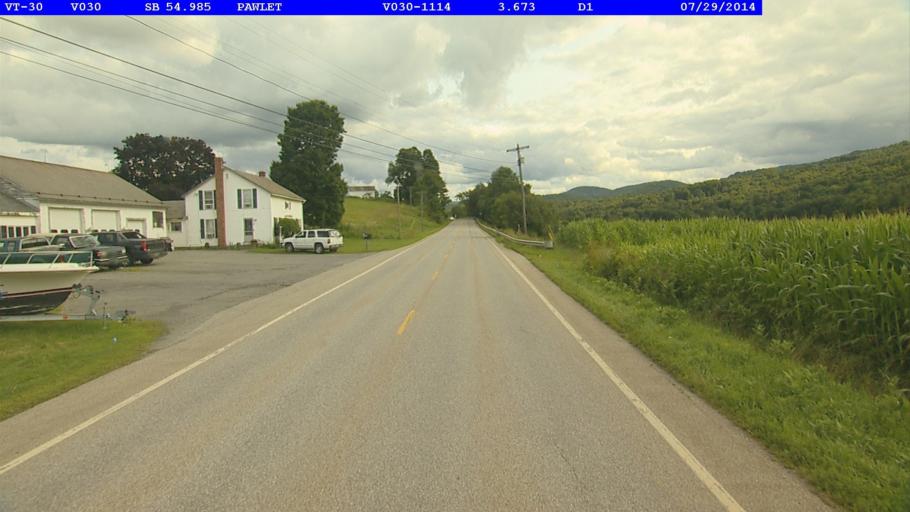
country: US
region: New York
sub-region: Washington County
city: Granville
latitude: 43.3599
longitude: -73.1842
